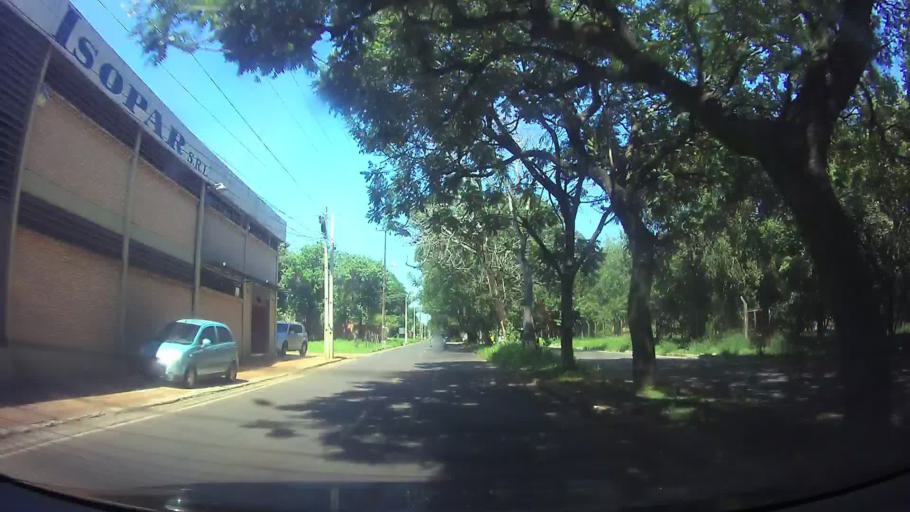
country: PY
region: Central
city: Fernando de la Mora
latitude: -25.2882
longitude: -57.5205
